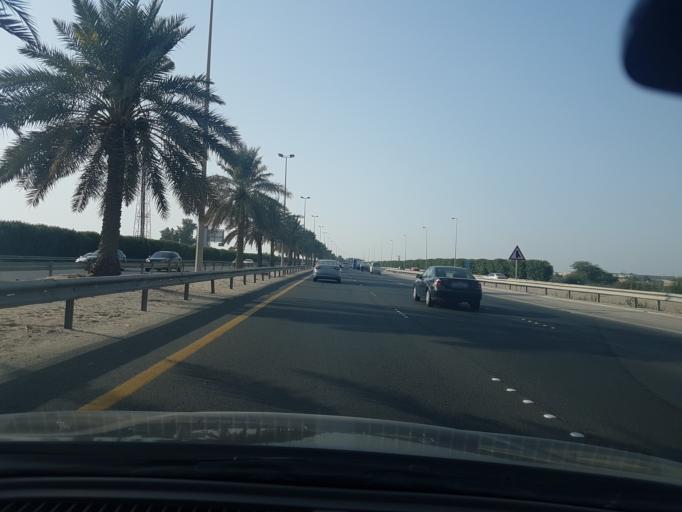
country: BH
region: Northern
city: Madinat `Isa
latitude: 26.1649
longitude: 50.5039
